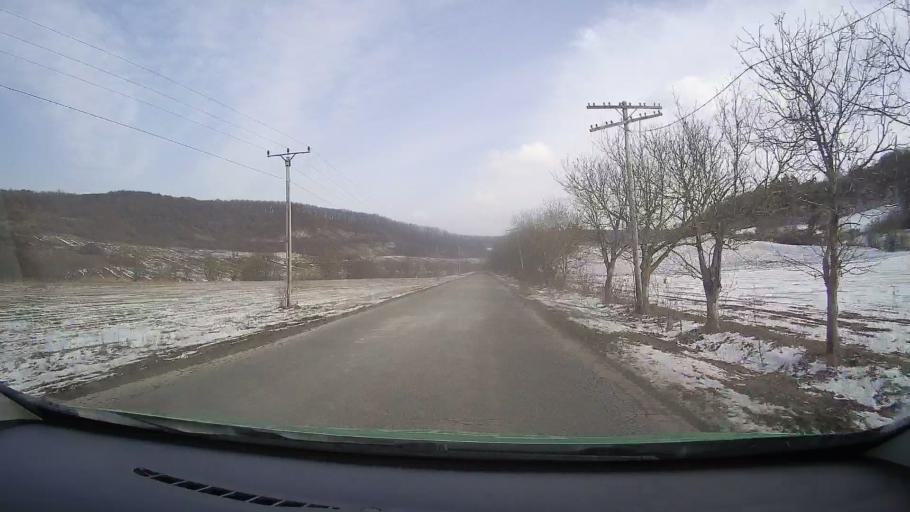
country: RO
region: Mures
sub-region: Comuna Apold
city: Apold
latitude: 46.1425
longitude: 24.8096
